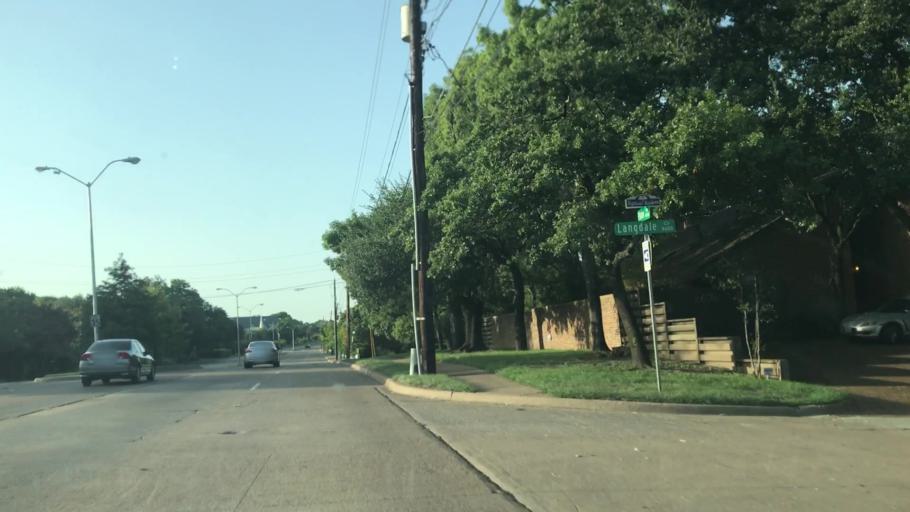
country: US
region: Texas
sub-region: Dallas County
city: Garland
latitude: 32.8671
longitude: -96.7003
